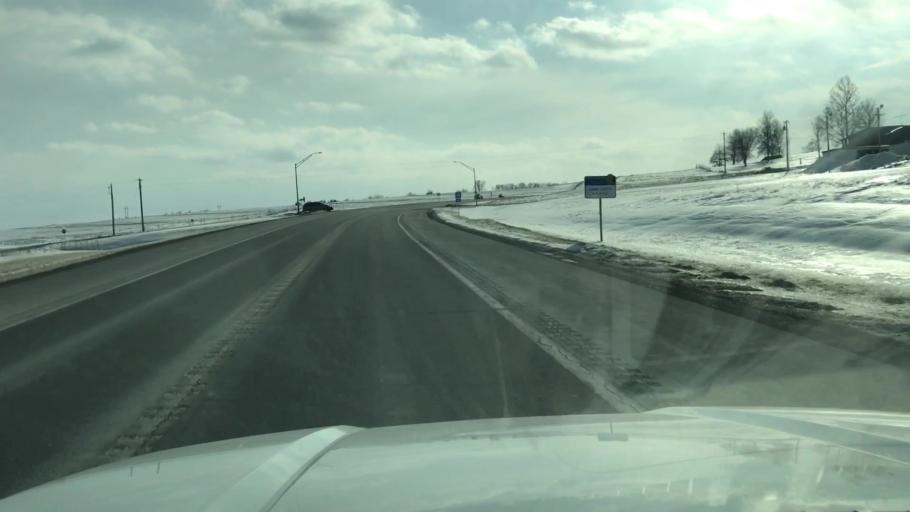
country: US
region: Missouri
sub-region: Nodaway County
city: Maryville
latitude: 40.3356
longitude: -94.8540
